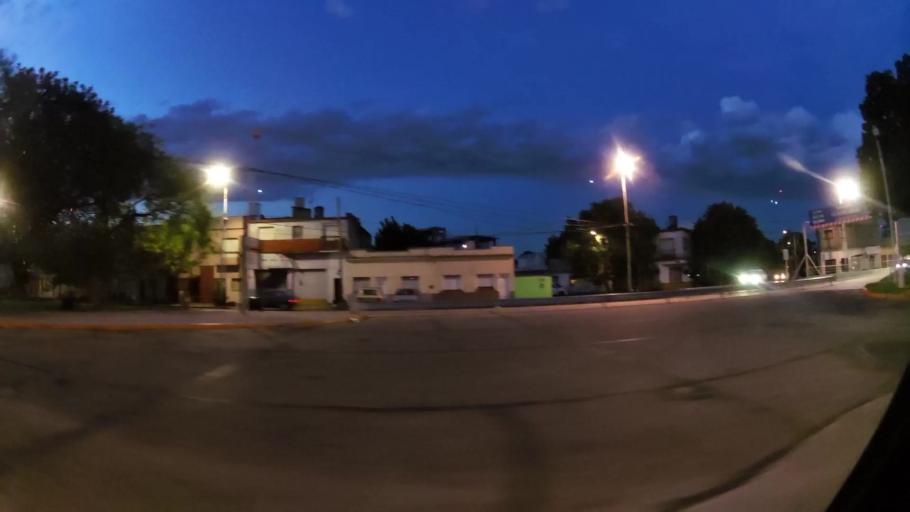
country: AR
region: Buenos Aires
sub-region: Partido de Avellaneda
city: Avellaneda
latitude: -34.6949
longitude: -58.3234
